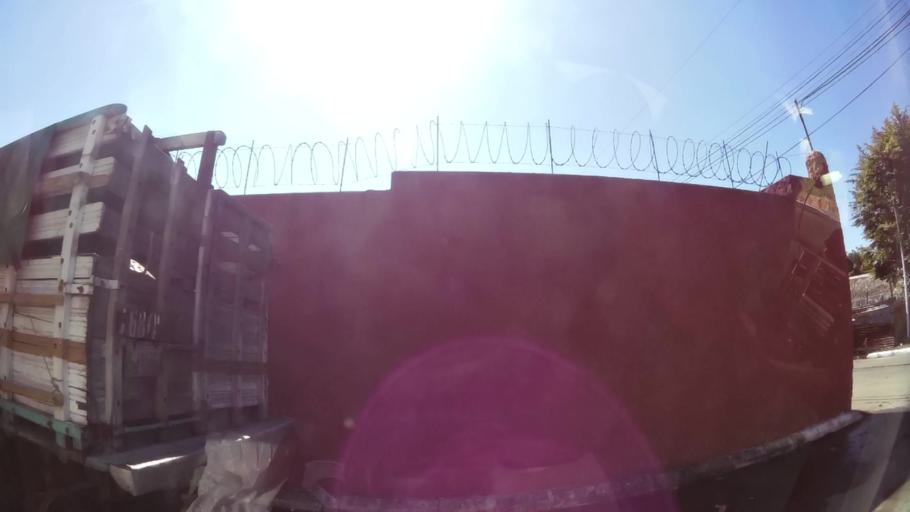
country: GT
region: Escuintla
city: Iztapa
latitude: 13.9311
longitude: -90.7132
